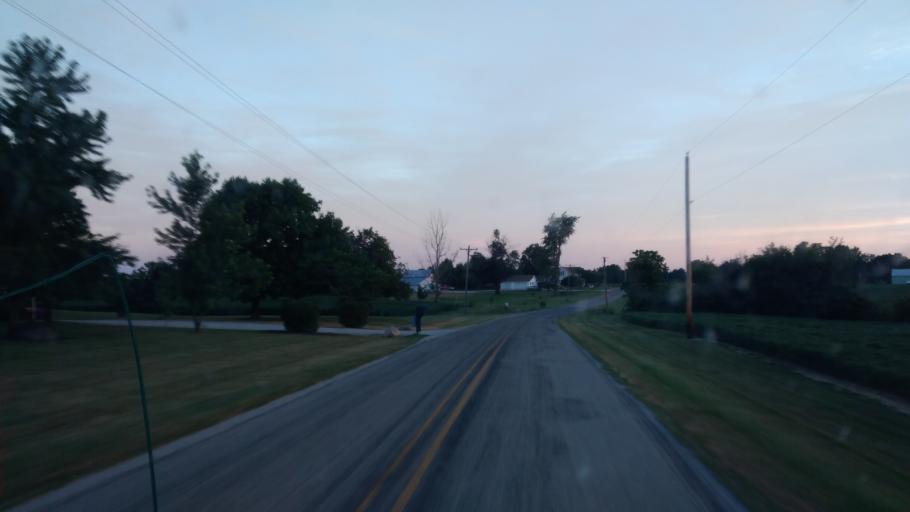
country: US
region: Indiana
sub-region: Wells County
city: Bluffton
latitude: 40.6815
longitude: -85.1353
